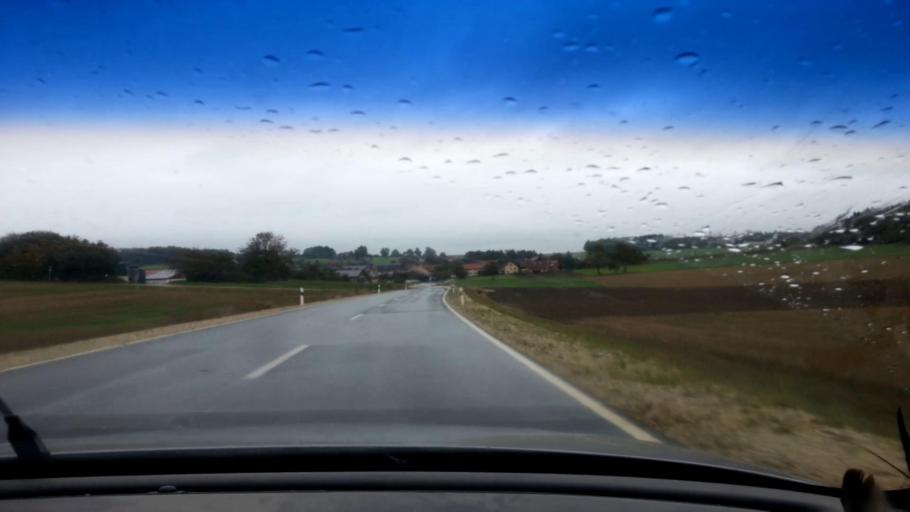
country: DE
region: Bavaria
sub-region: Upper Franconia
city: Poxdorf
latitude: 49.9316
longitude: 11.0801
